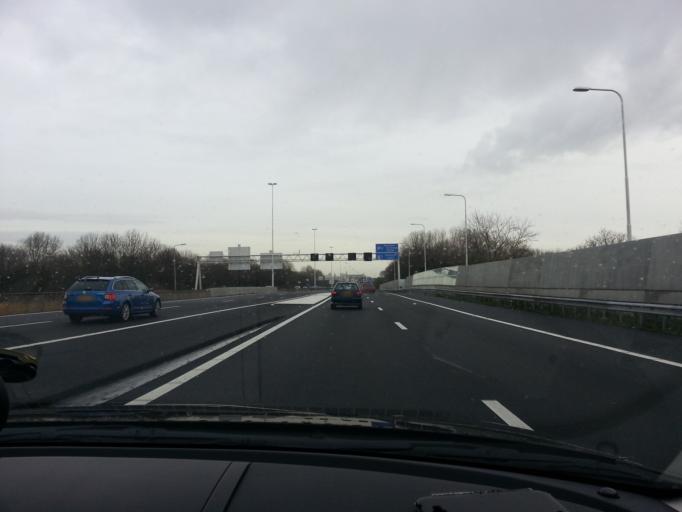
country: NL
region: South Holland
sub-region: Gemeente Schiedam
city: Schiedam
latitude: 51.9260
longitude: 4.3805
